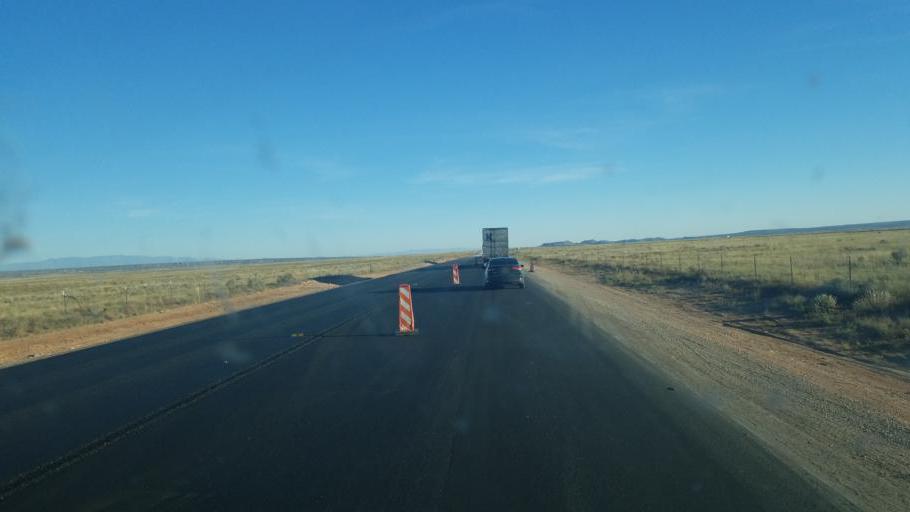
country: US
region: New Mexico
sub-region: Valencia County
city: Los Lunas
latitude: 34.8818
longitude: -107.0607
